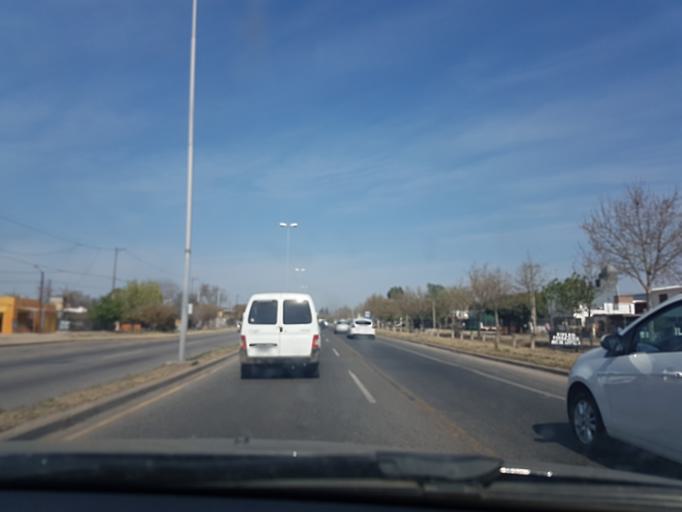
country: AR
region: Cordoba
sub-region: Departamento de Capital
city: Cordoba
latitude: -31.4798
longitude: -64.2396
